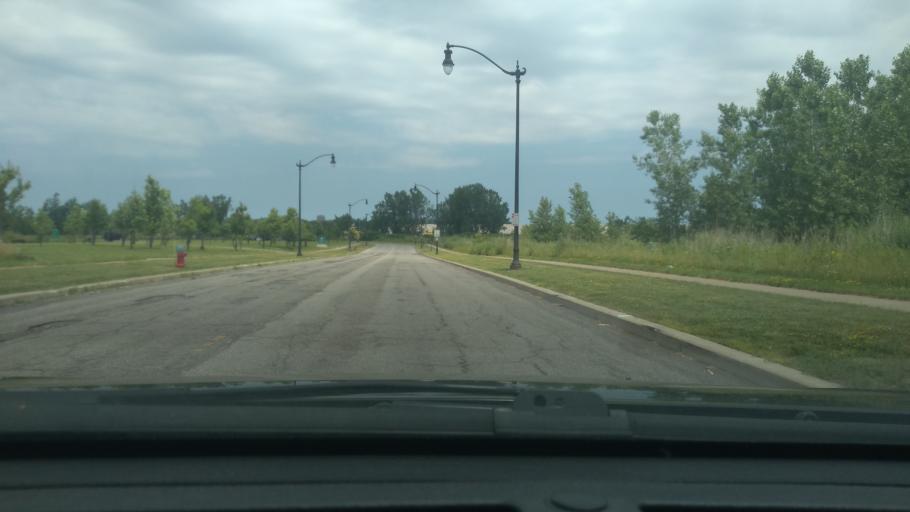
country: US
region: New York
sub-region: Erie County
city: Lackawanna
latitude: 42.8352
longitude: -78.8452
